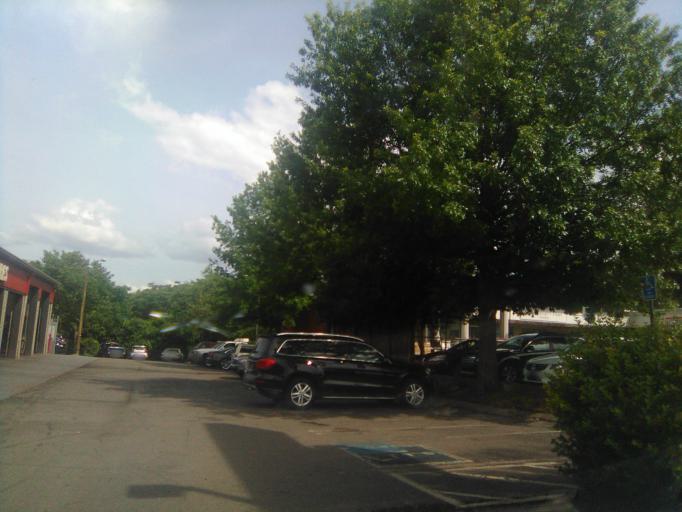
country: US
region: Tennessee
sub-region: Davidson County
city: Belle Meade
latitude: 36.0983
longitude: -86.8721
